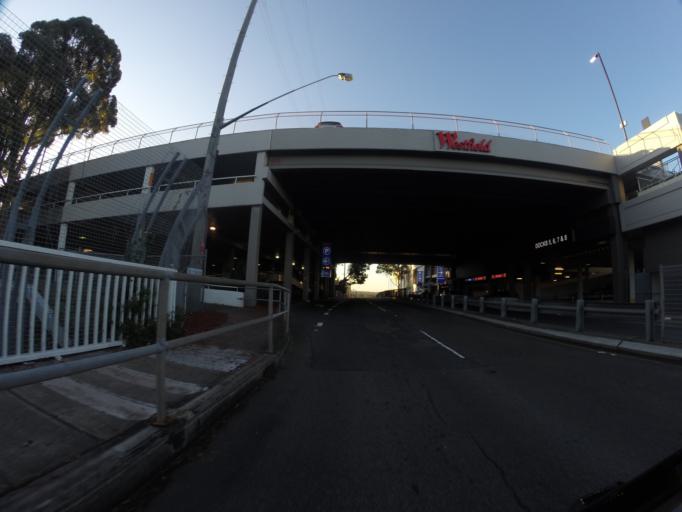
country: AU
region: New South Wales
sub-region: Sutherland Shire
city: Miranda
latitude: -34.0357
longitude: 151.0983
